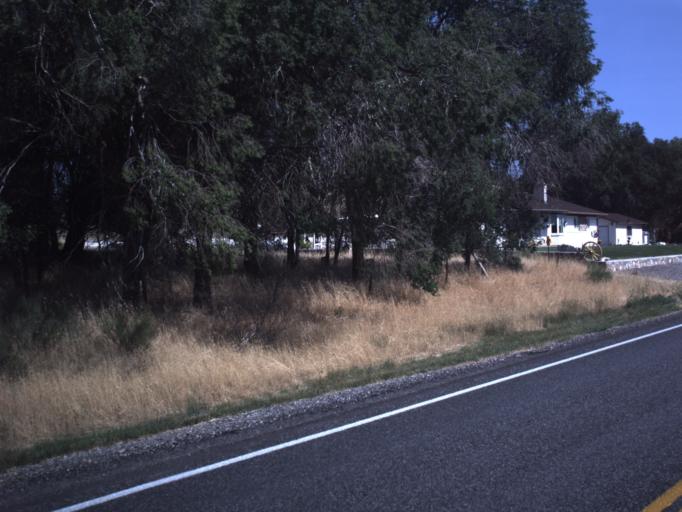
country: US
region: Utah
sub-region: Sanpete County
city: Moroni
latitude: 39.5301
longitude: -111.5451
